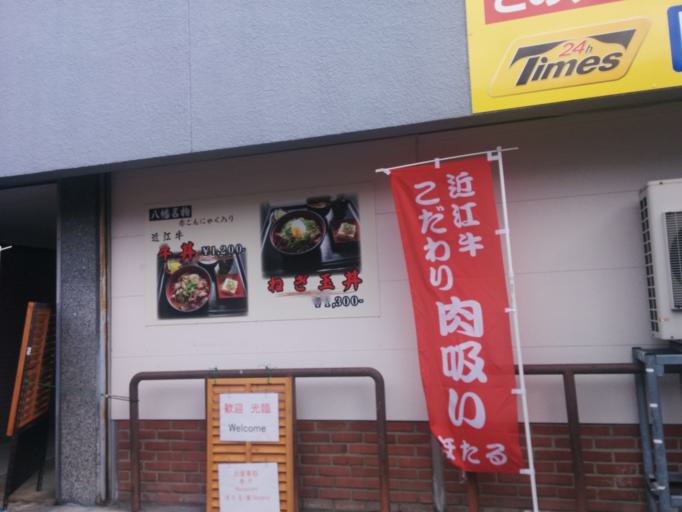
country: JP
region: Shiga Prefecture
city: Omihachiman
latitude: 35.1387
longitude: 136.0923
